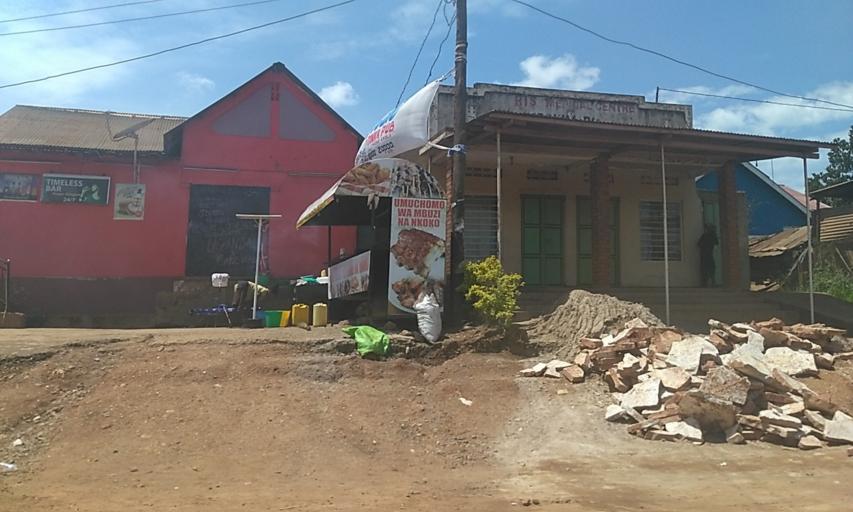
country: UG
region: Central Region
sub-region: Wakiso District
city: Wakiso
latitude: 0.3798
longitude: 32.5194
